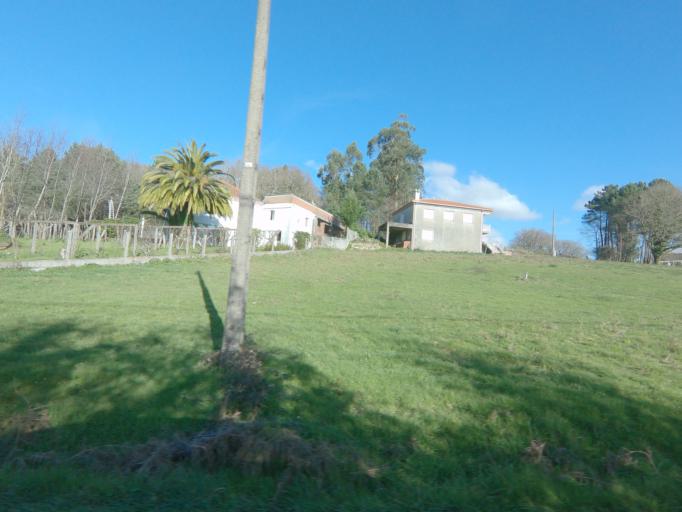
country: ES
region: Galicia
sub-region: Provincia da Coruna
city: Ribeira
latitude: 42.7039
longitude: -8.4273
